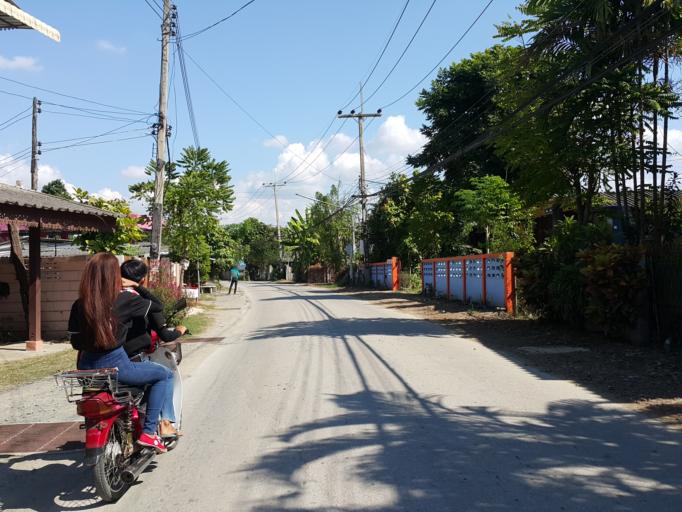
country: TH
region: Chiang Mai
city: San Kamphaeng
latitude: 18.7738
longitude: 99.1169
